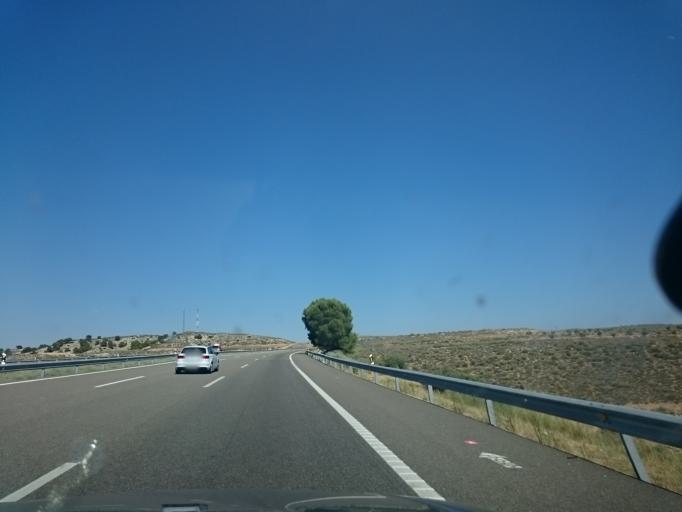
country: ES
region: Aragon
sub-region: Provincia de Huesca
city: Penalba
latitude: 41.5135
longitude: -0.0296
